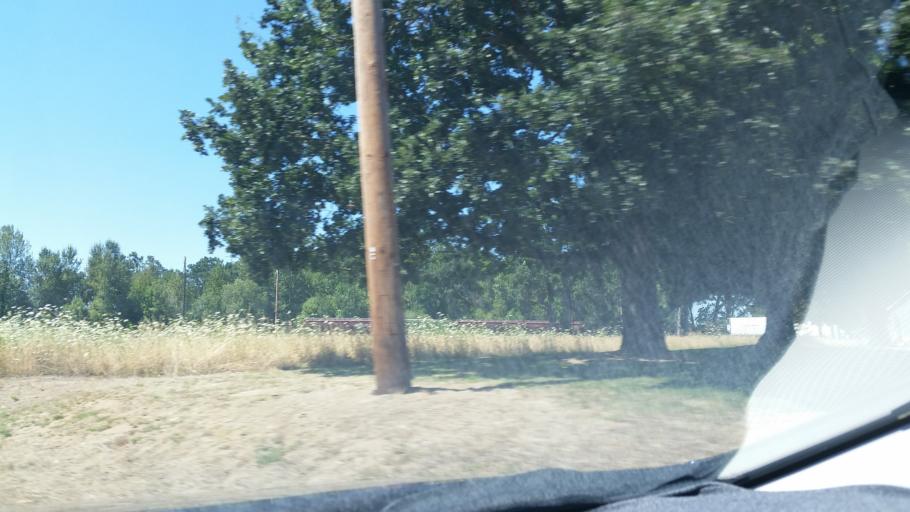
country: US
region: Oregon
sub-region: Clackamas County
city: Wilsonville
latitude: 45.2596
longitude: -122.8017
